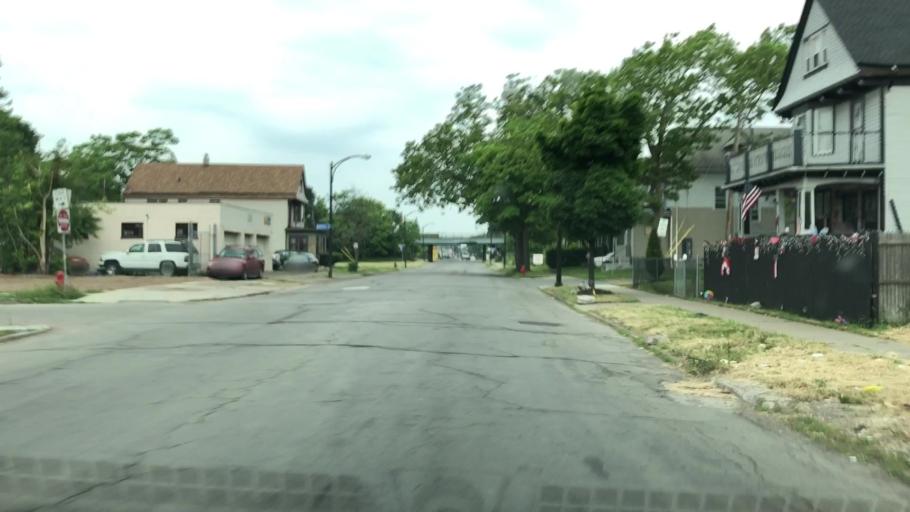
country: US
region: New York
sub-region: Erie County
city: Sloan
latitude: 42.9035
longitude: -78.8269
